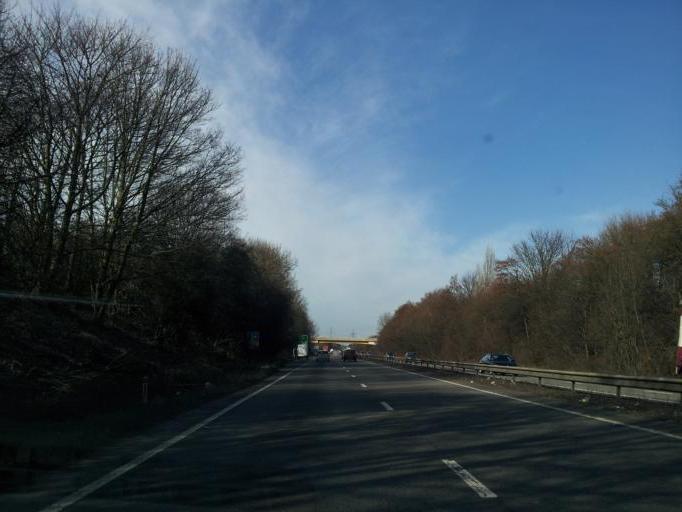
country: GB
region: England
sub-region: Lincolnshire
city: Barrowby
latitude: 52.9074
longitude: -0.6742
